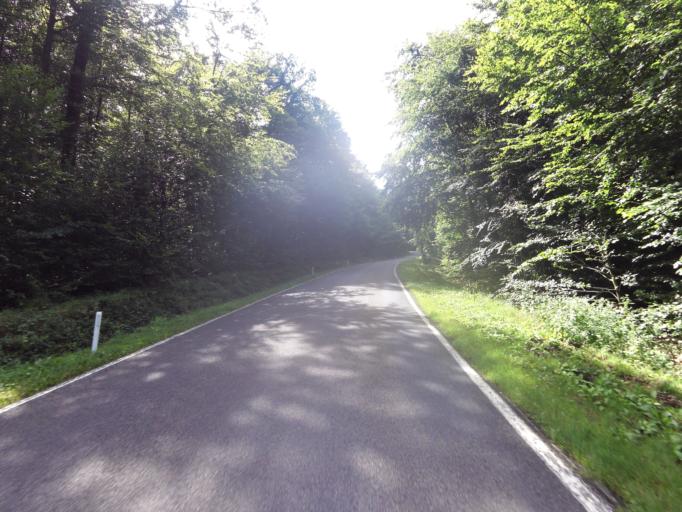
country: BE
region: Wallonia
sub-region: Province du Luxembourg
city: Saint-Hubert
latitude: 50.0691
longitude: 5.3474
